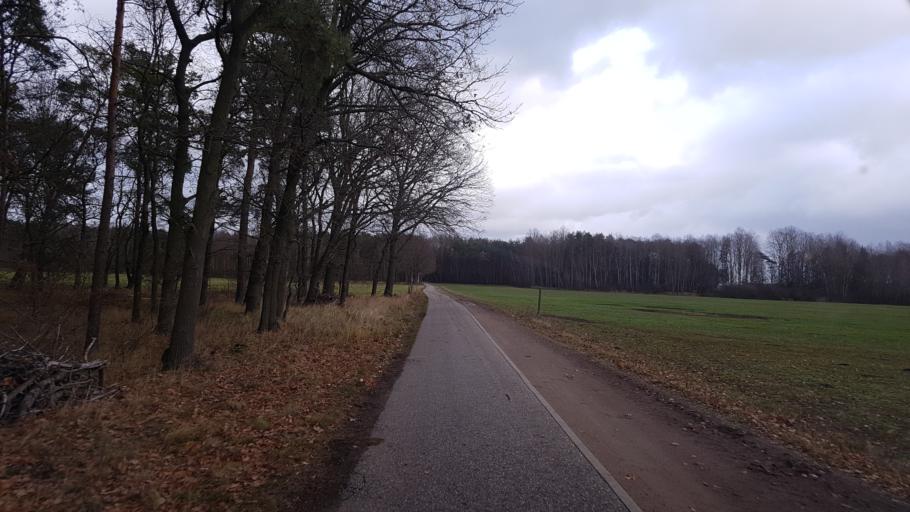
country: DE
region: Brandenburg
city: Finsterwalde
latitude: 51.5990
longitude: 13.6487
